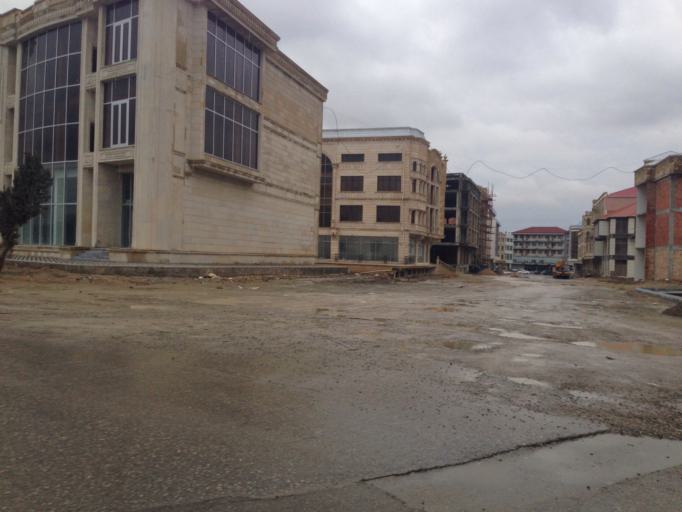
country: AZ
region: Baki
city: Baku
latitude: 40.4076
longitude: 49.8601
